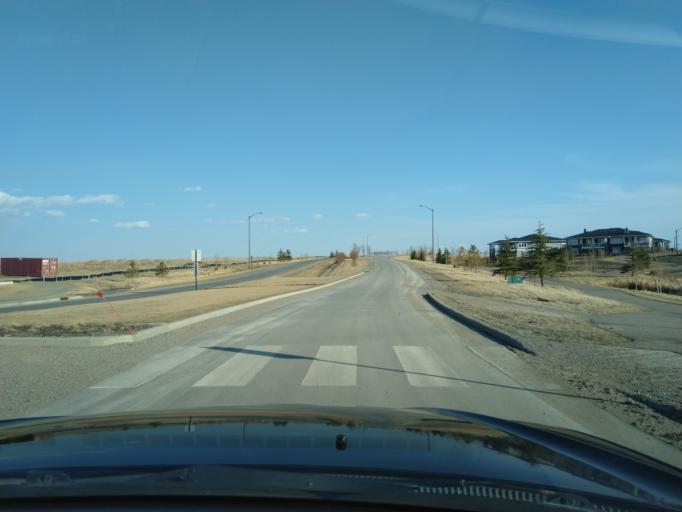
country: CA
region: Alberta
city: Cochrane
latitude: 51.1131
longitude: -114.3932
